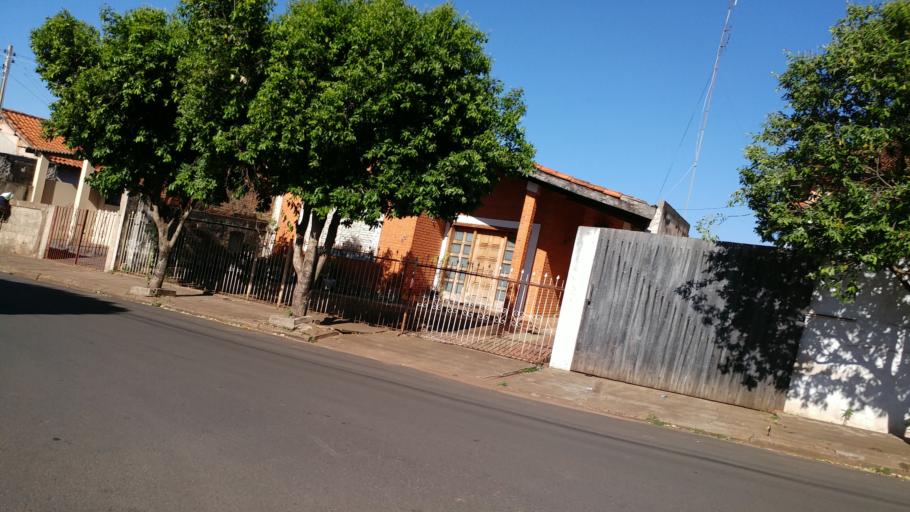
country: BR
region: Sao Paulo
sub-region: Paraguacu Paulista
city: Paraguacu Paulista
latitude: -22.4248
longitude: -50.5807
